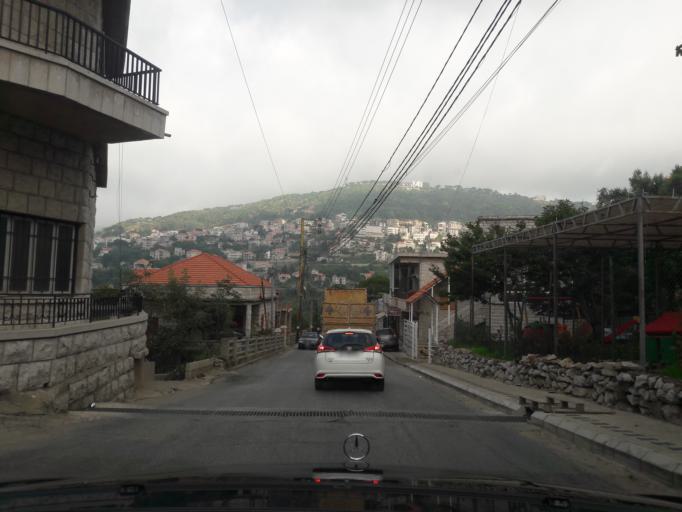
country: LB
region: Mont-Liban
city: Djounie
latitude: 33.9293
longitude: 35.7297
